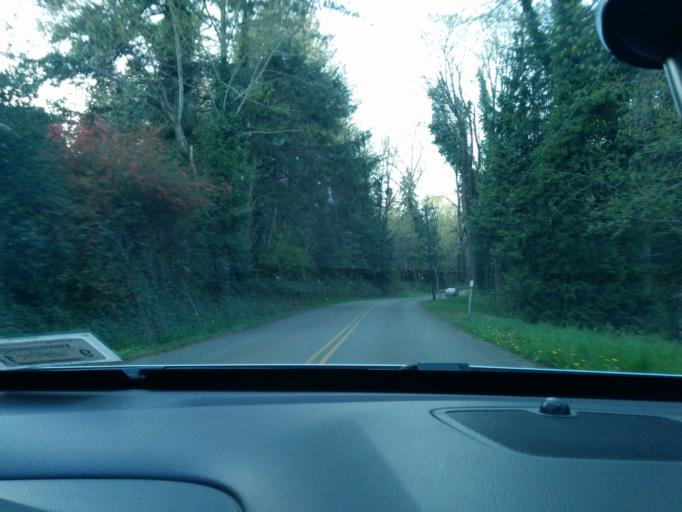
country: US
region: Washington
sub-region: Snohomish County
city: Gold Bar
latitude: 47.8741
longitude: -121.7337
